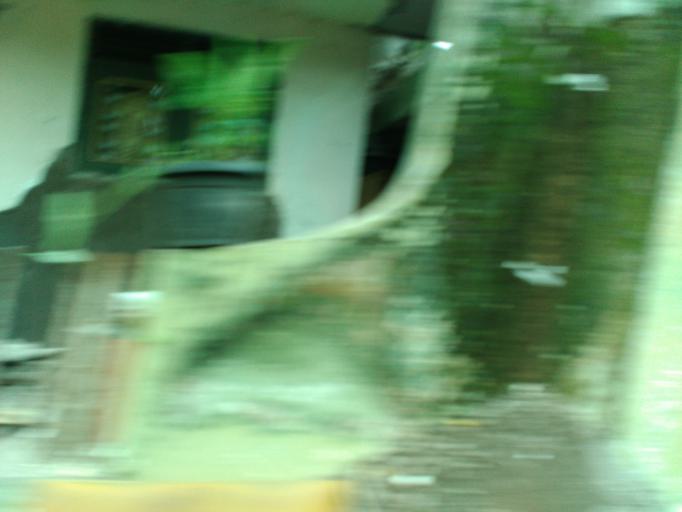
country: ID
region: Central Java
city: Delanggu
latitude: -7.6193
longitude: 110.7017
